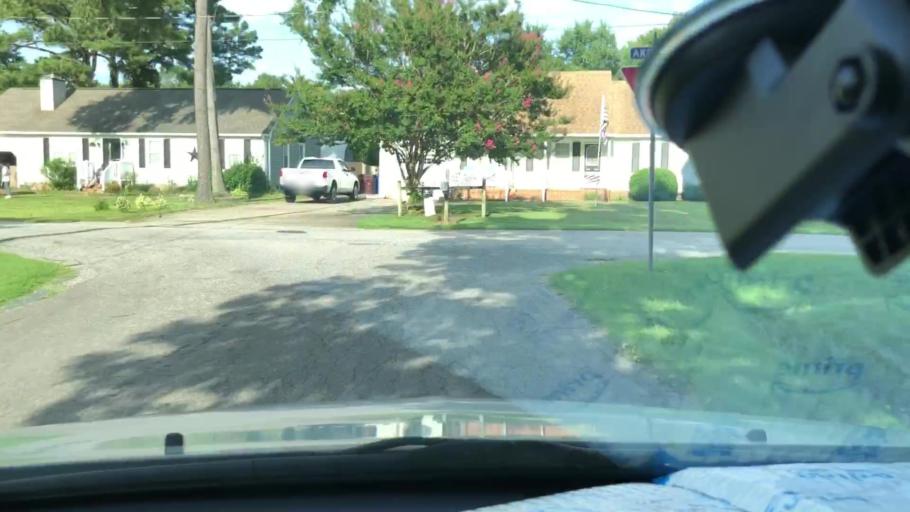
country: US
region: Virginia
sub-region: City of Chesapeake
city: Chesapeake
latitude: 36.7050
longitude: -76.2752
